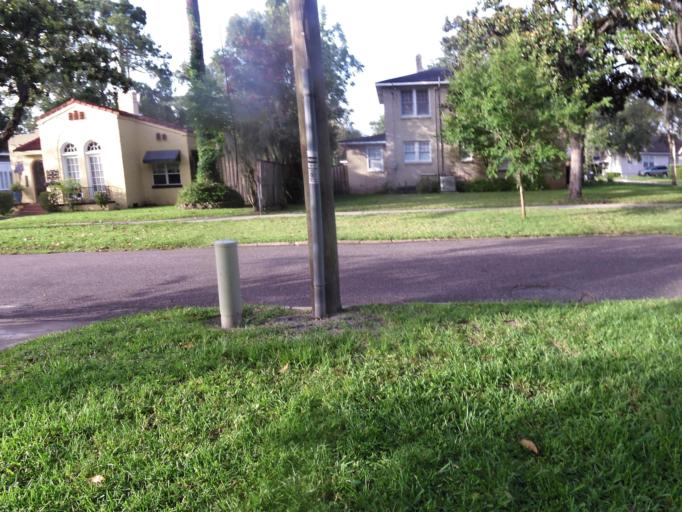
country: US
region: Florida
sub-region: Duval County
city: Jacksonville
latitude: 30.3008
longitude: -81.7070
